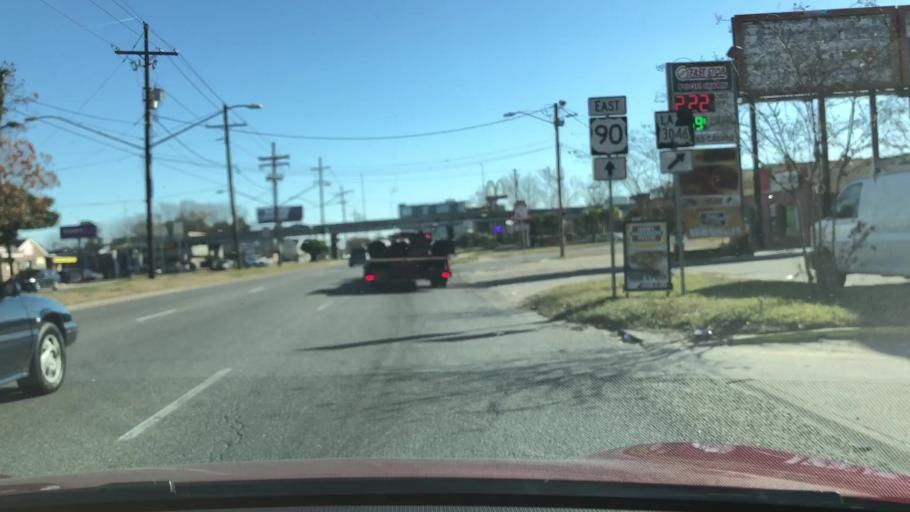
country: US
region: Louisiana
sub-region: Jefferson Parish
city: Jefferson
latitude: 29.9630
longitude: -90.1585
